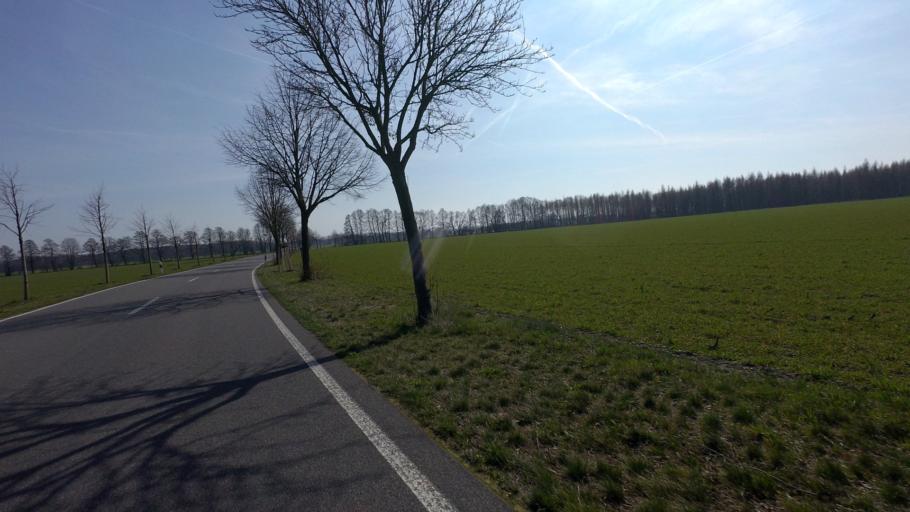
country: DE
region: Brandenburg
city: Golssen
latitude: 51.9507
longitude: 13.5956
